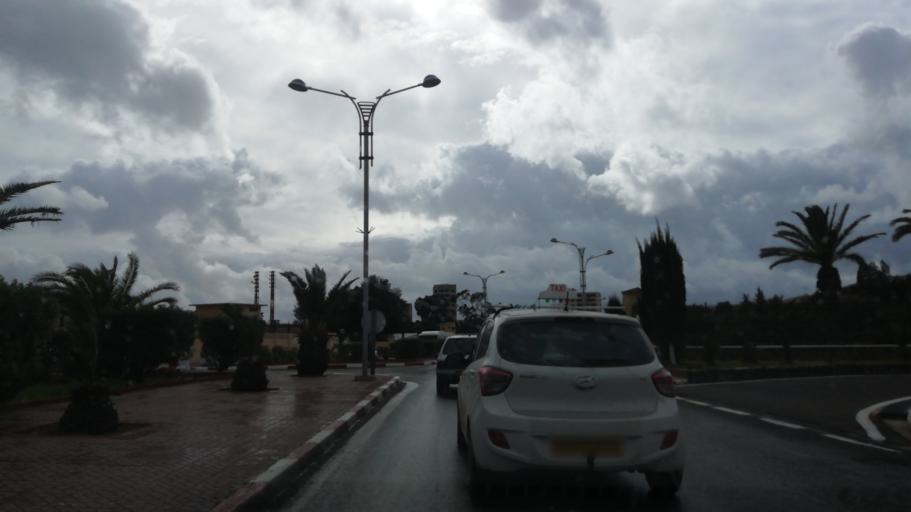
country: DZ
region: Oran
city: Oran
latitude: 35.6832
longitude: -0.6710
